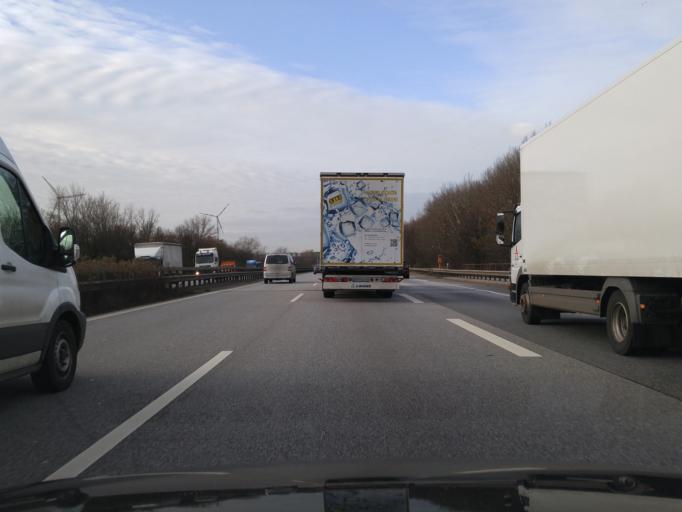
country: DE
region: Hamburg
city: Rothenburgsort
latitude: 53.5095
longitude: 10.0550
